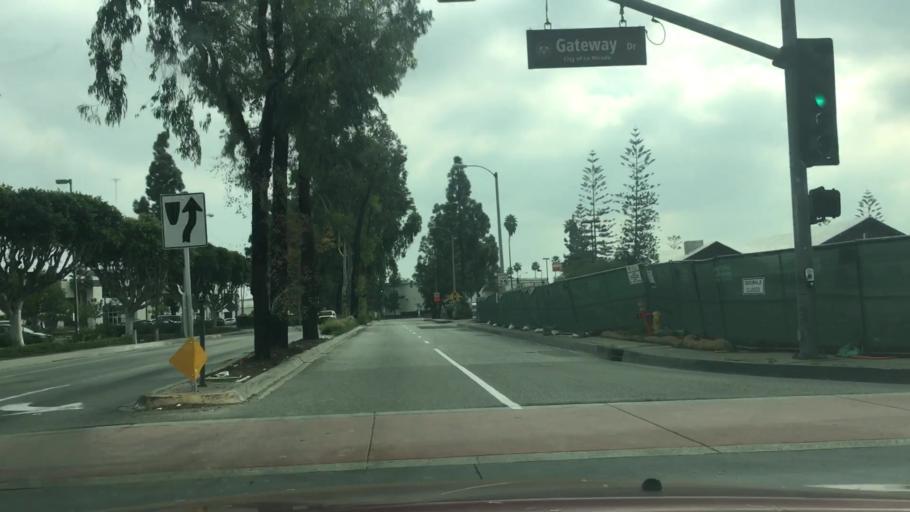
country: US
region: California
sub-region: Orange County
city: Buena Park
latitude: 33.8846
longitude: -118.0272
